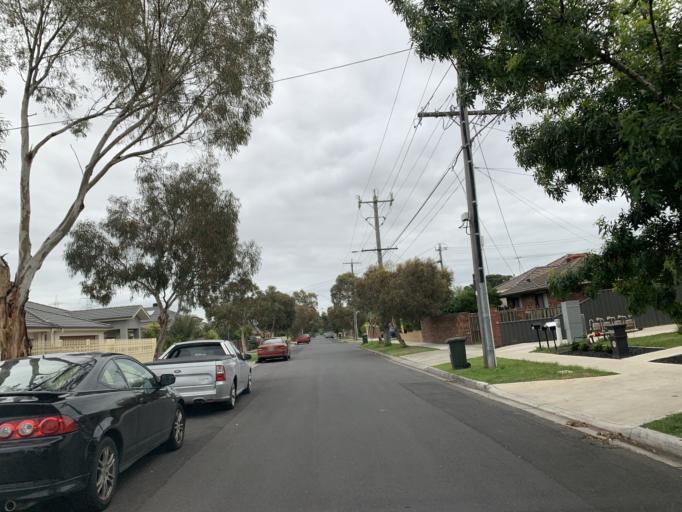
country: AU
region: Victoria
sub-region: Brimbank
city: St Albans
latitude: -37.7476
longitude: 144.7965
